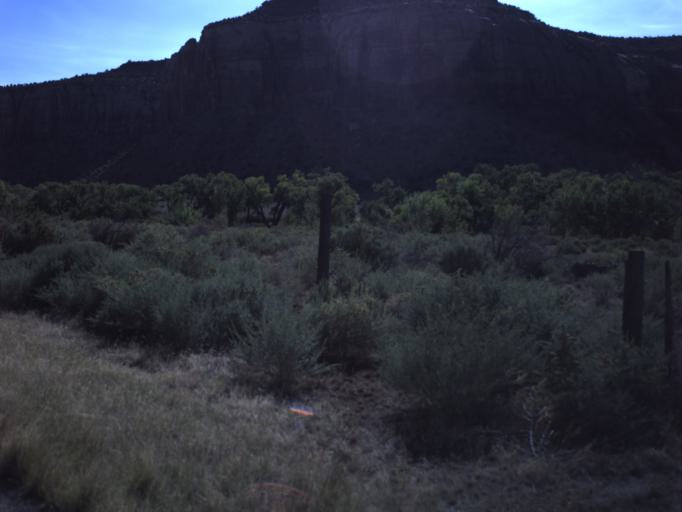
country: US
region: Utah
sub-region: San Juan County
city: Monticello
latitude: 38.0514
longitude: -109.5527
